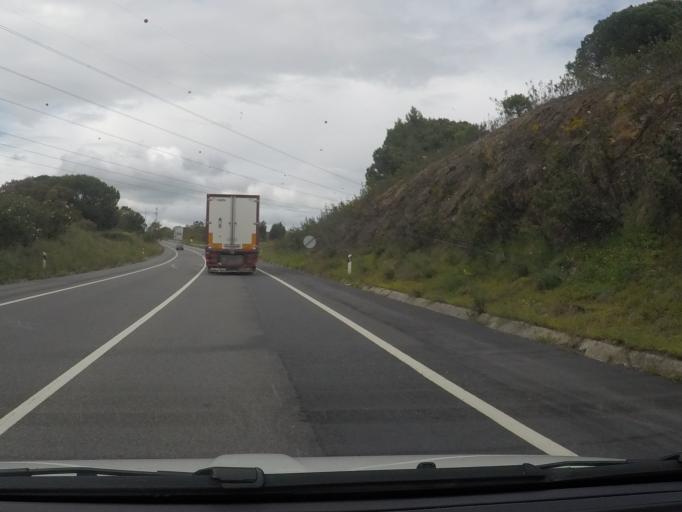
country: PT
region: Setubal
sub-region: Santiago do Cacem
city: Santiago do Cacem
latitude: 38.0796
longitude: -8.6426
